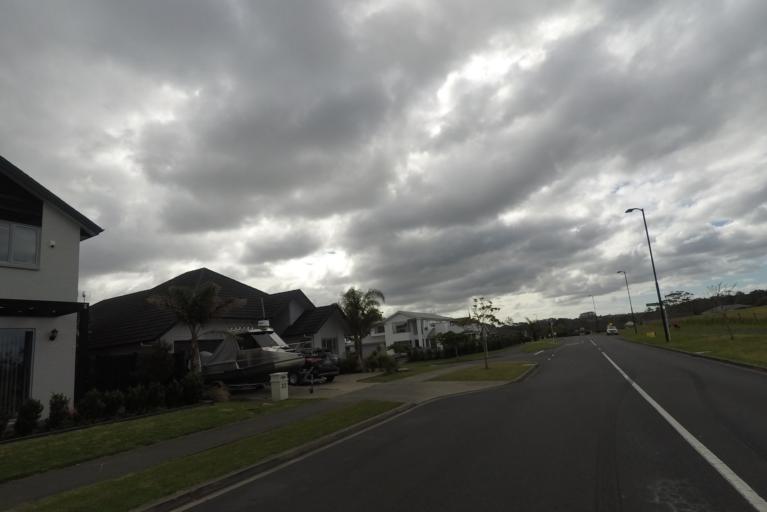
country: NZ
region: Auckland
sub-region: Auckland
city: Rothesay Bay
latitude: -36.6023
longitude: 174.6687
